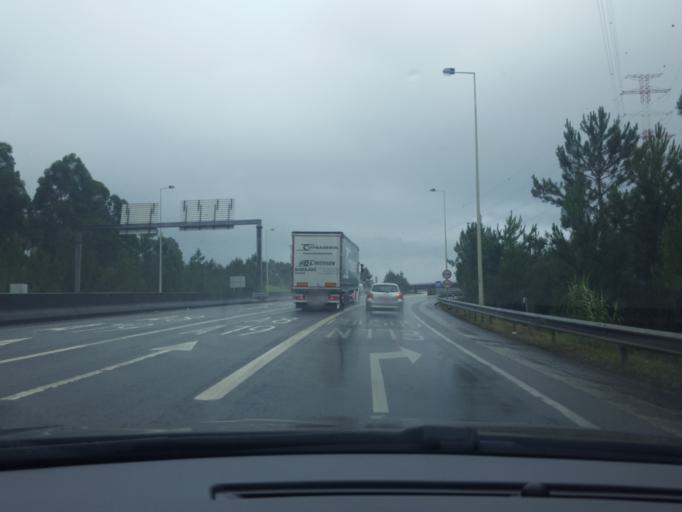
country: PT
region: Leiria
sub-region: Leiria
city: Leiria
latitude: 39.7397
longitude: -8.7687
